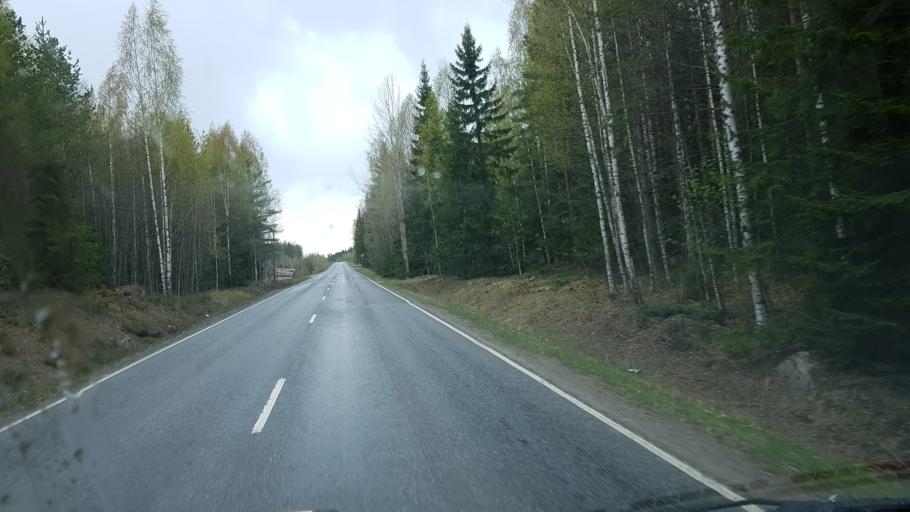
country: FI
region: Pirkanmaa
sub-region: Tampere
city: Pirkkala
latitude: 61.3997
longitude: 23.6293
